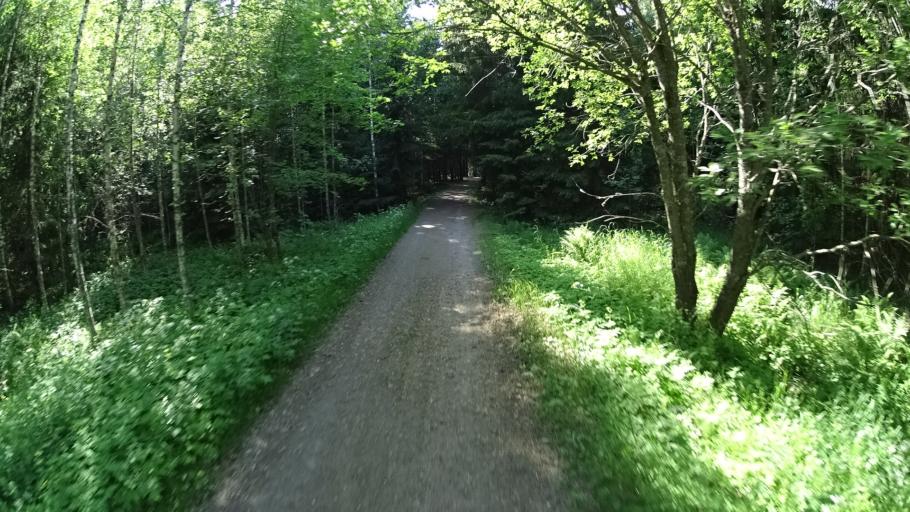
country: FI
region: Uusimaa
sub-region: Helsinki
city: Vantaa
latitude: 60.2367
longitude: 25.1731
